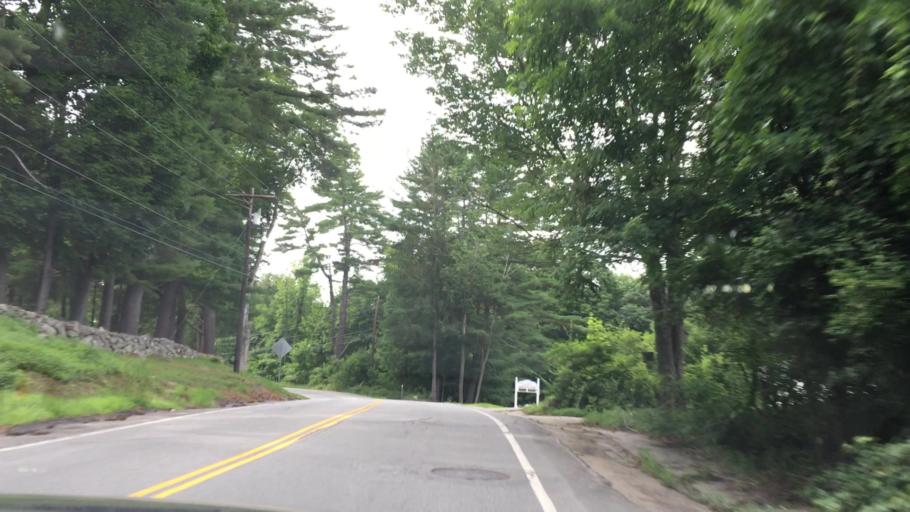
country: US
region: New Hampshire
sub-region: Carroll County
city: Center Harbor
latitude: 43.7109
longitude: -71.4670
